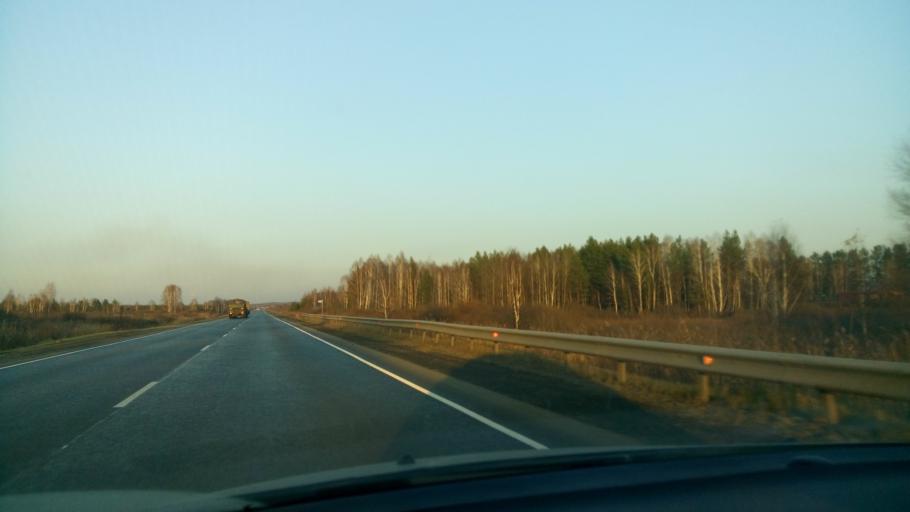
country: RU
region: Sverdlovsk
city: Yelanskiy
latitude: 56.8247
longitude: 62.5547
